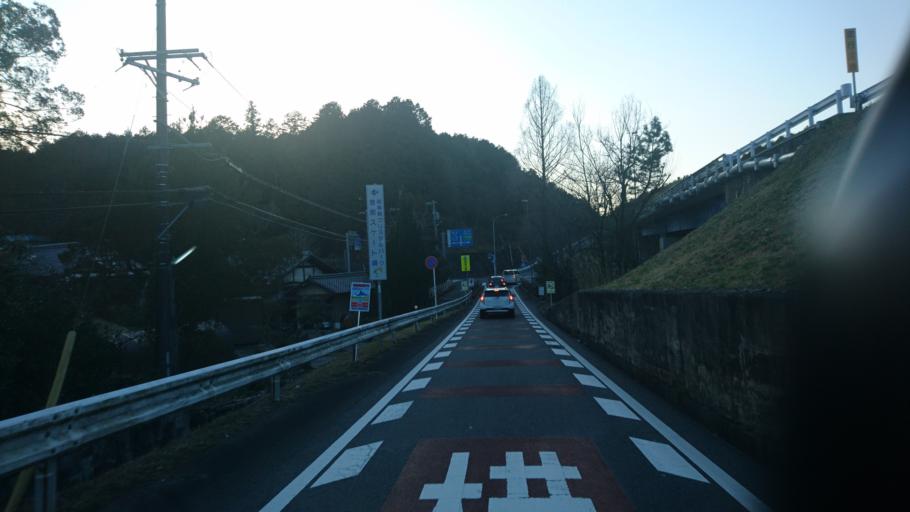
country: JP
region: Gifu
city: Nakatsugawa
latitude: 35.4476
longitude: 137.4007
